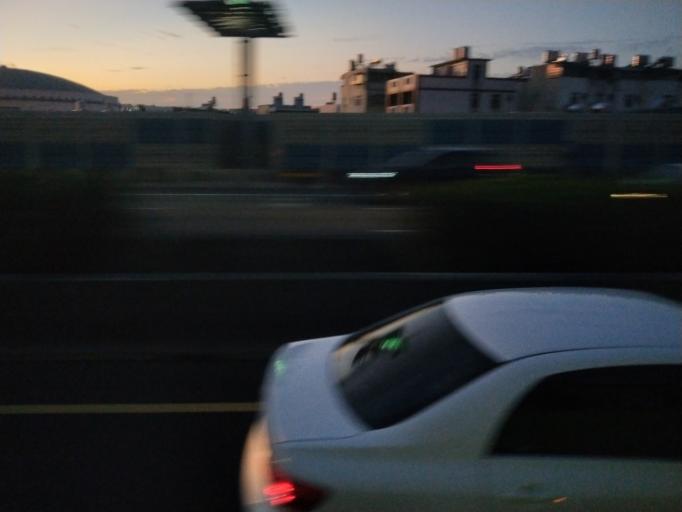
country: TW
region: Taiwan
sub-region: Taichung City
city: Taichung
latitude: 24.1967
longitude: 120.6434
